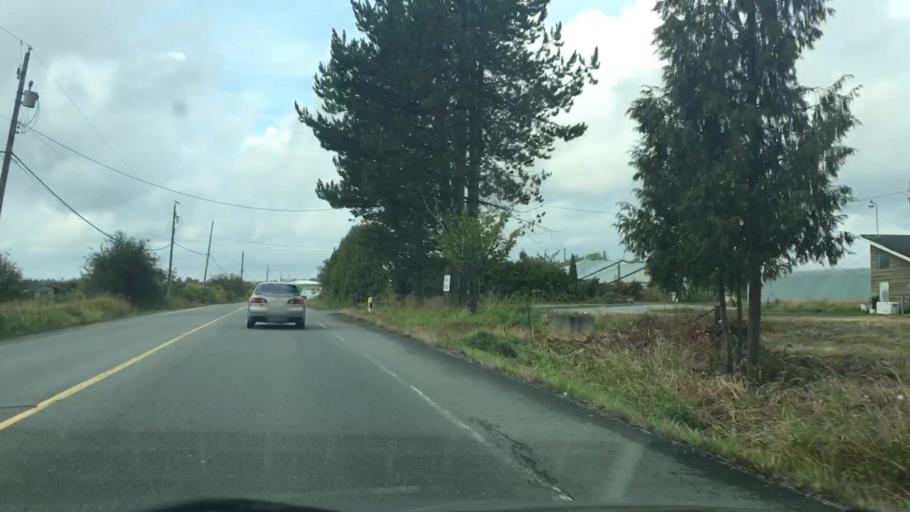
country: CA
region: British Columbia
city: Langley
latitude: 49.1042
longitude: -122.6138
